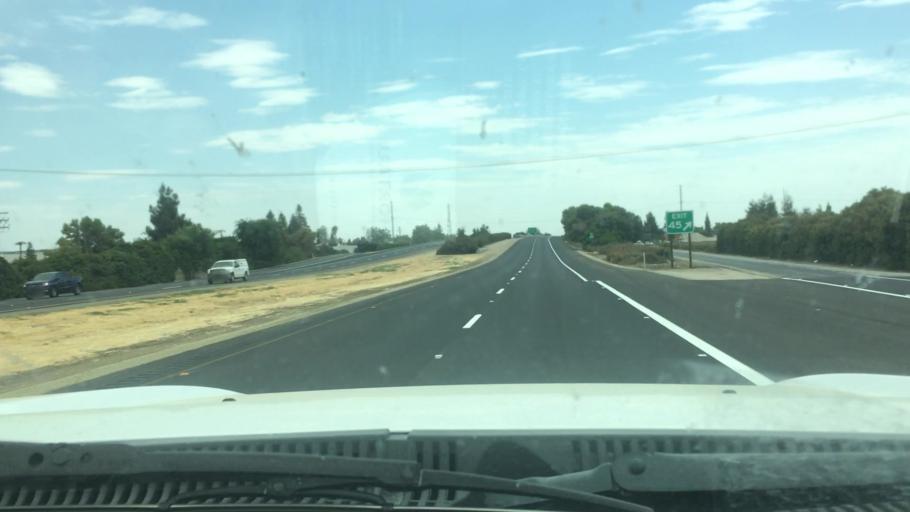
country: US
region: California
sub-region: Tulare County
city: Porterville
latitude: 36.0847
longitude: -119.0394
